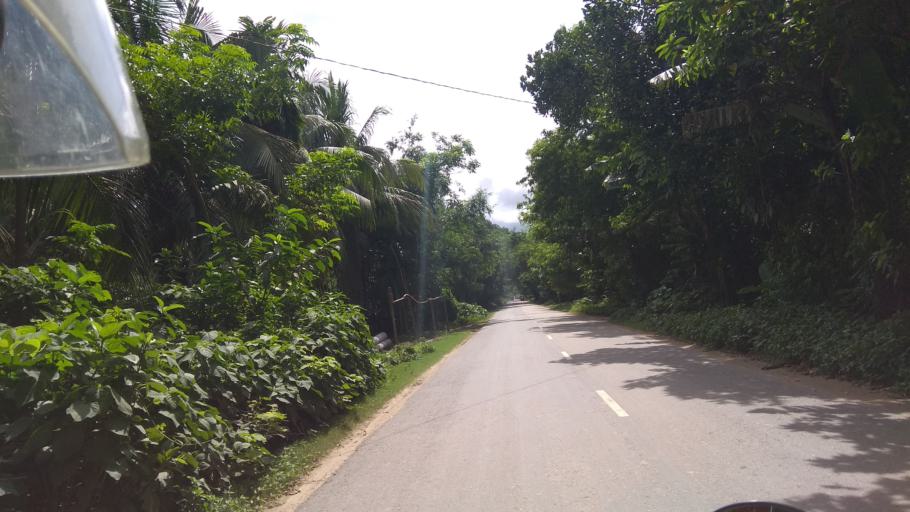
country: BD
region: Khulna
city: Kalia
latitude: 23.1957
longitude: 89.6804
